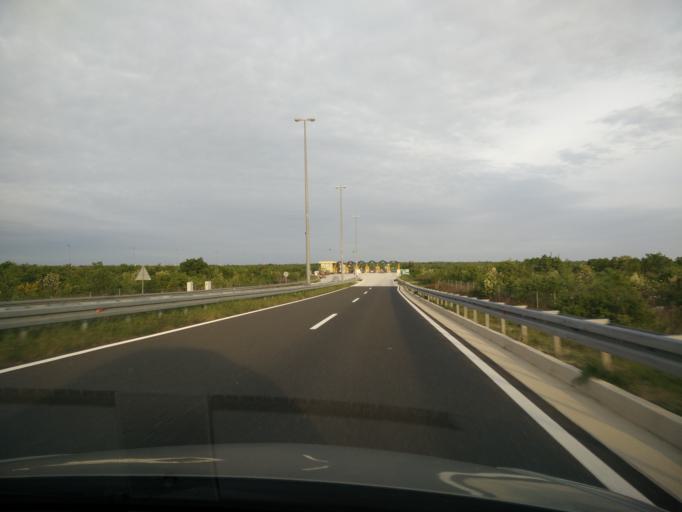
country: HR
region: Zadarska
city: Galovac
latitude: 44.1164
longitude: 15.4335
